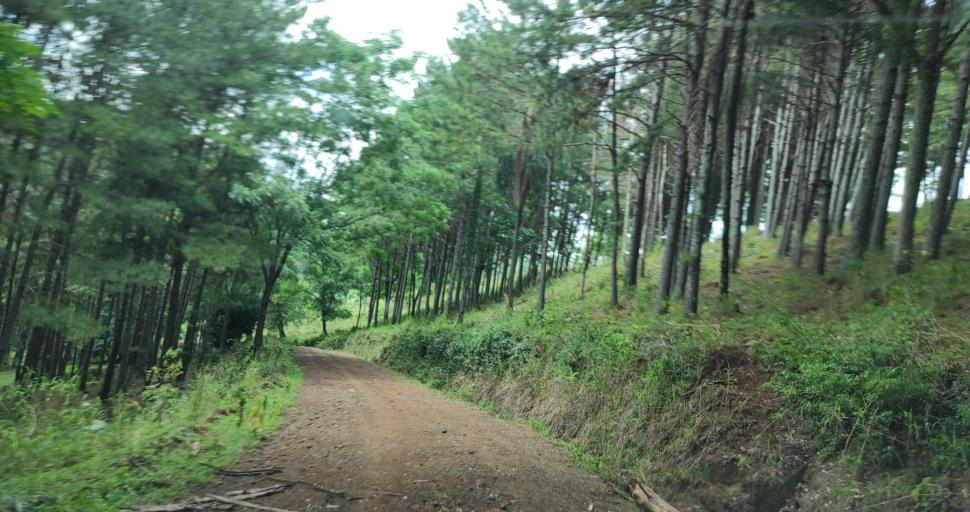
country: AR
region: Misiones
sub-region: Departamento de Veinticinco de Mayo
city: Veinticinco de Mayo
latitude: -27.4169
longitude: -54.7176
